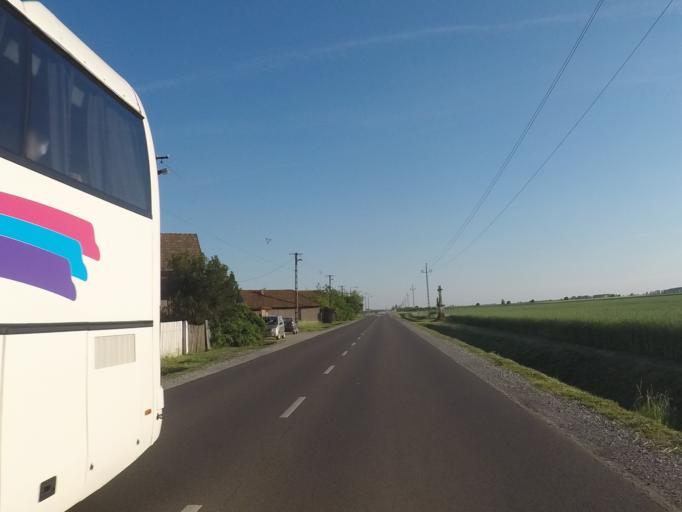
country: HU
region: Heves
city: Besenyotelek
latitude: 47.7181
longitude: 20.4139
